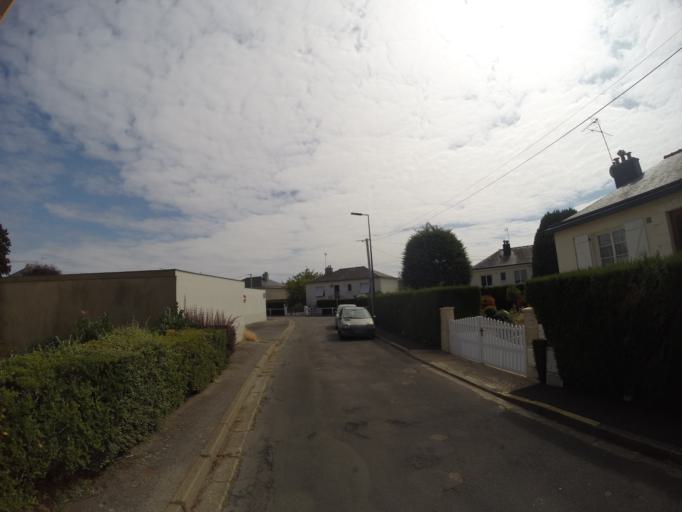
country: FR
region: Centre
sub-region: Departement d'Indre-et-Loire
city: Saint-Cyr-sur-Loire
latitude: 47.4162
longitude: 0.6944
